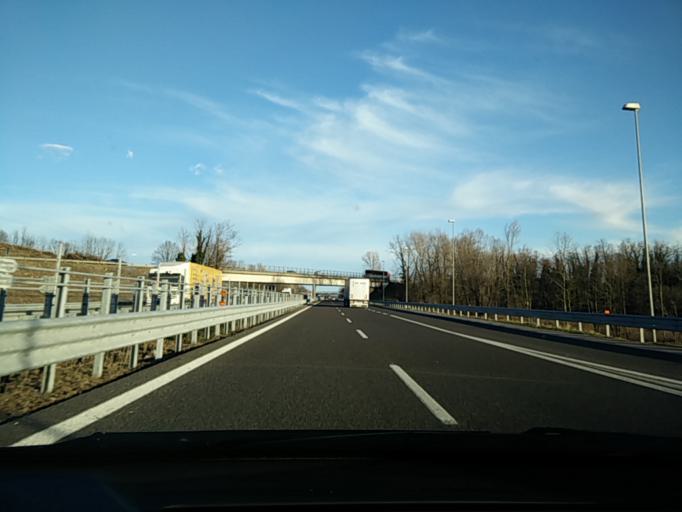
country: IT
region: Friuli Venezia Giulia
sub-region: Provincia di Udine
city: Santo Stefano
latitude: 46.1856
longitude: 13.1211
